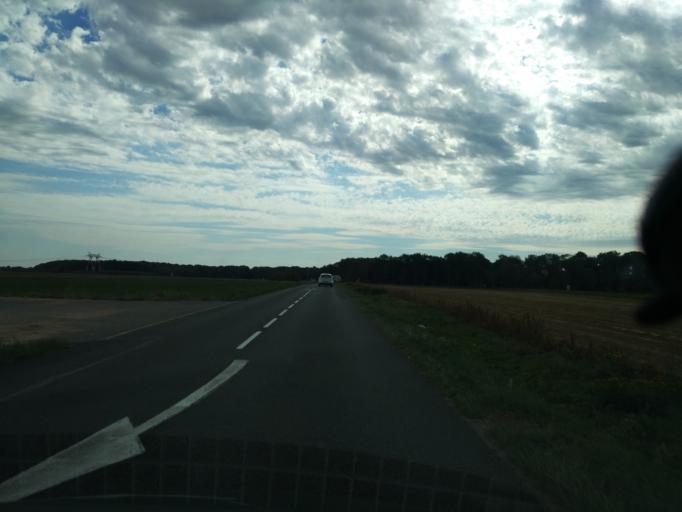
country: FR
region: Ile-de-France
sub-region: Departement de l'Essonne
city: Briis-sous-Forges
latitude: 48.6446
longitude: 2.1209
